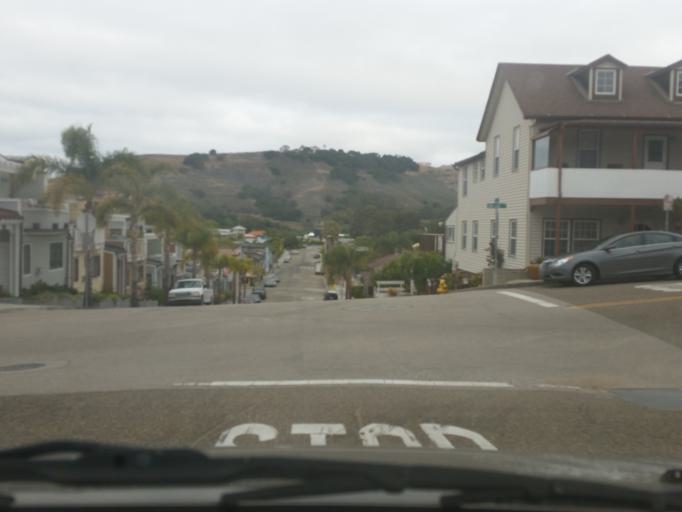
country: US
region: California
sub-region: San Luis Obispo County
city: Avila Beach
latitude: 35.1793
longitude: -120.7321
